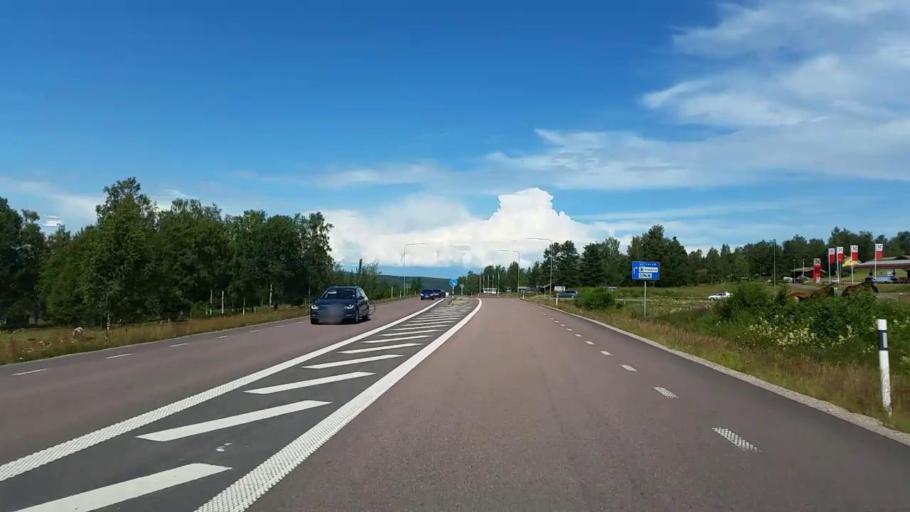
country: SE
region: Dalarna
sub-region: Rattviks Kommun
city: Raettvik
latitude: 60.8589
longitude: 15.1023
